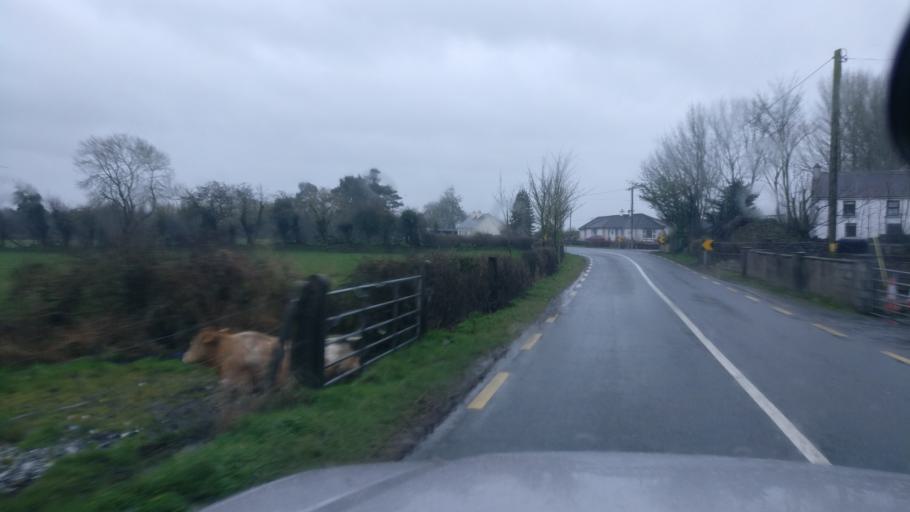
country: IE
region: Connaught
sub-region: County Galway
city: Ballinasloe
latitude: 53.2465
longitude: -8.1755
